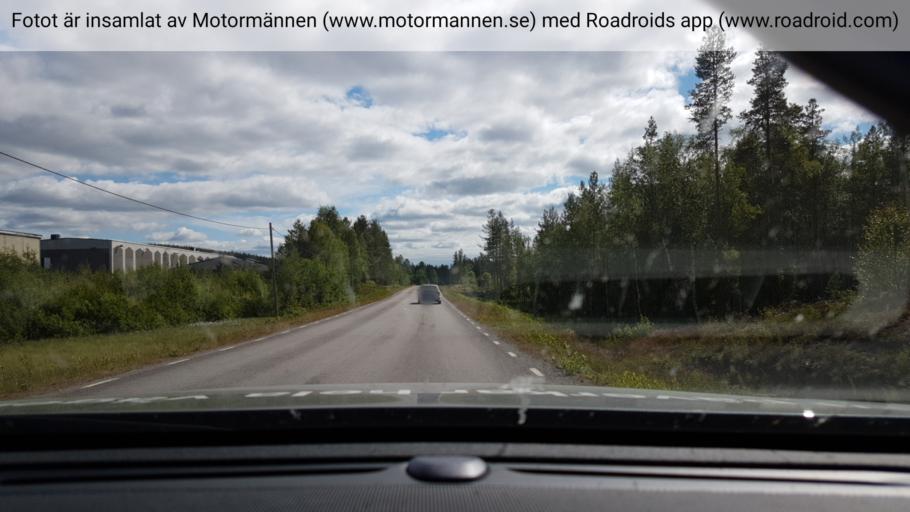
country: SE
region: Vaesterbotten
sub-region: Sorsele Kommun
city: Sorsele
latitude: 65.5695
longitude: 17.5238
